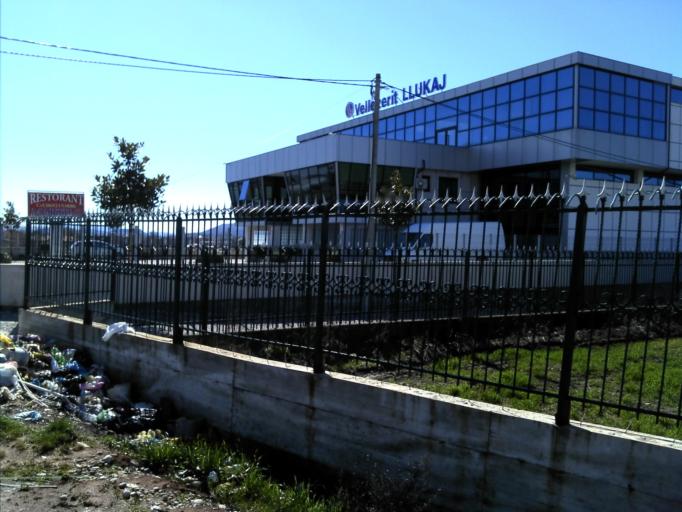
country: AL
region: Shkoder
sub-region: Rrethi i Shkodres
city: Shkoder
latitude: 42.1089
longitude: 19.5020
